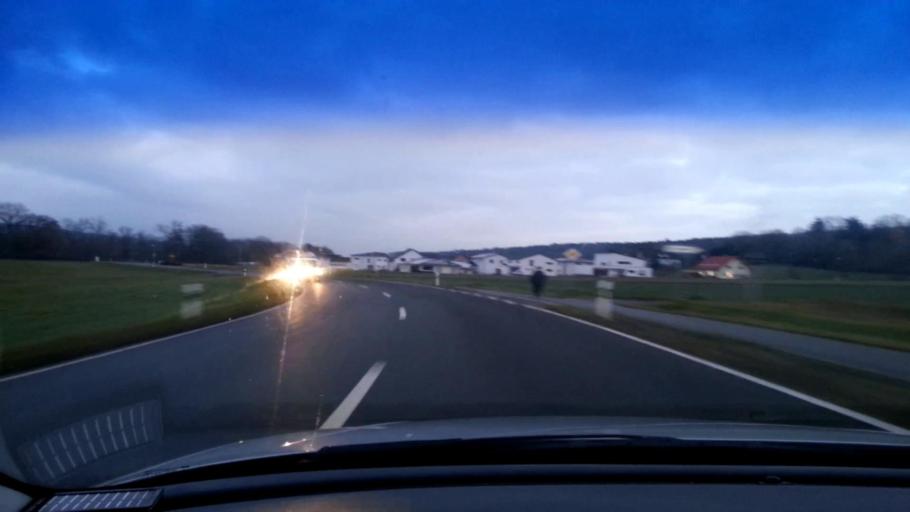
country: DE
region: Bavaria
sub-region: Upper Franconia
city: Frensdorf
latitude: 49.8490
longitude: 10.8887
